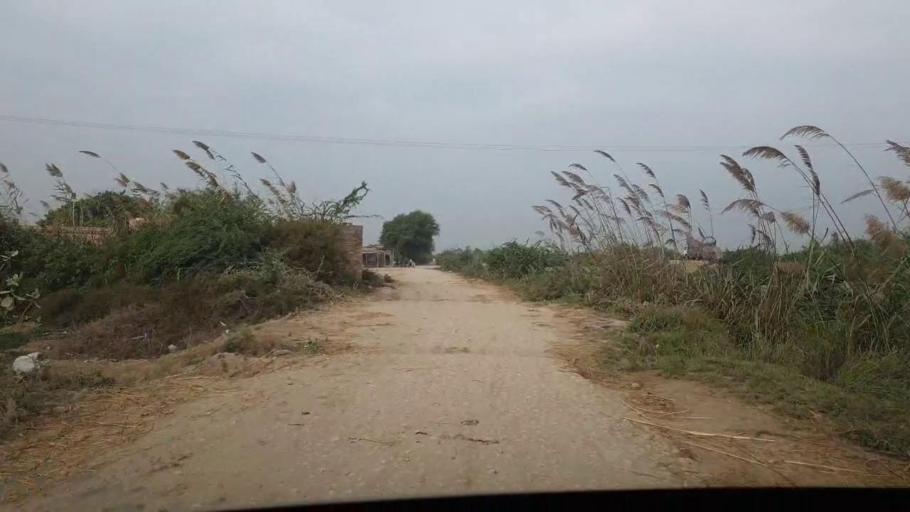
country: PK
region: Sindh
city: Chuhar Jamali
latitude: 24.4137
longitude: 67.9418
